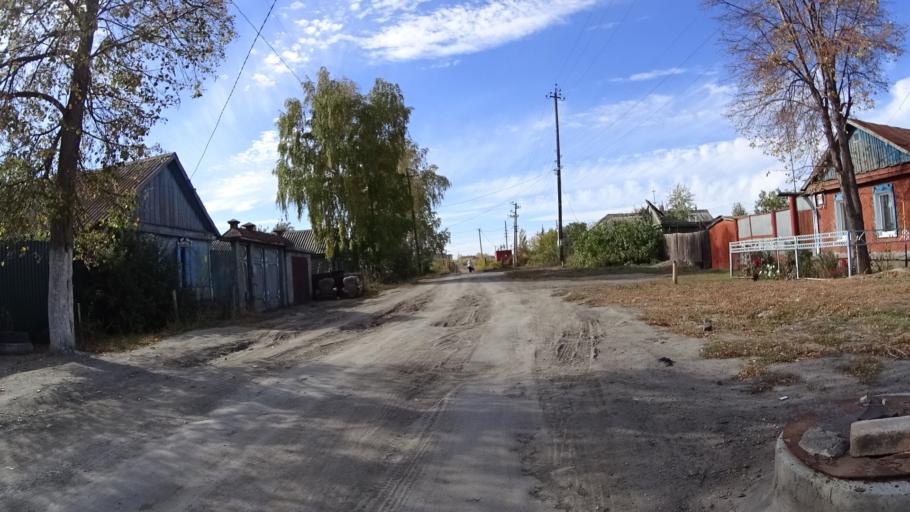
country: RU
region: Chelyabinsk
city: Troitsk
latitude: 54.0756
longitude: 61.5844
